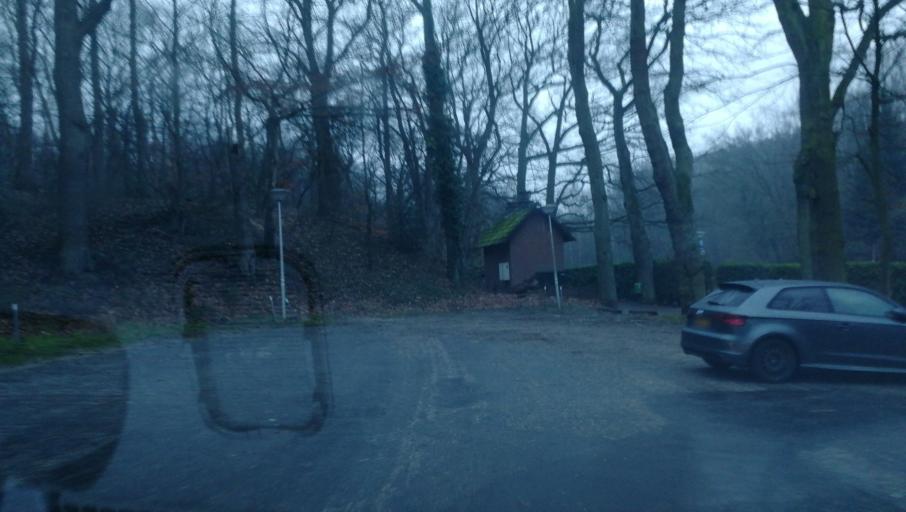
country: NL
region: Limburg
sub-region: Gemeente Venlo
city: Venlo
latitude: 51.3500
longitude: 6.1757
